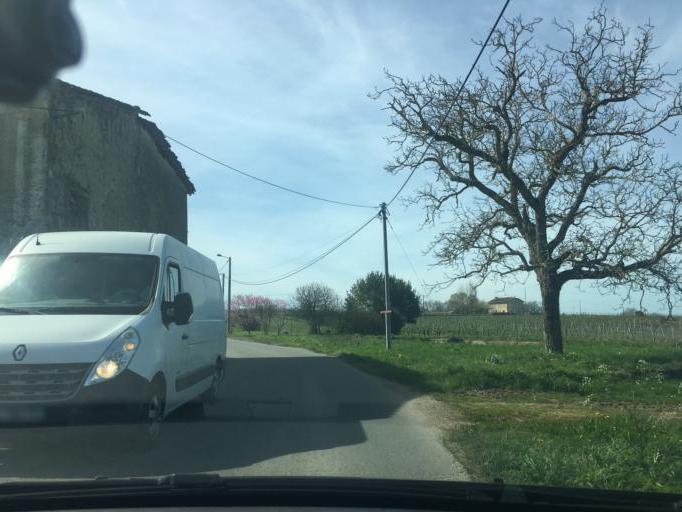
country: FR
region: Aquitaine
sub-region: Departement de la Gironde
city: Saint-Germain-du-Puch
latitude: 44.8485
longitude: -0.3428
